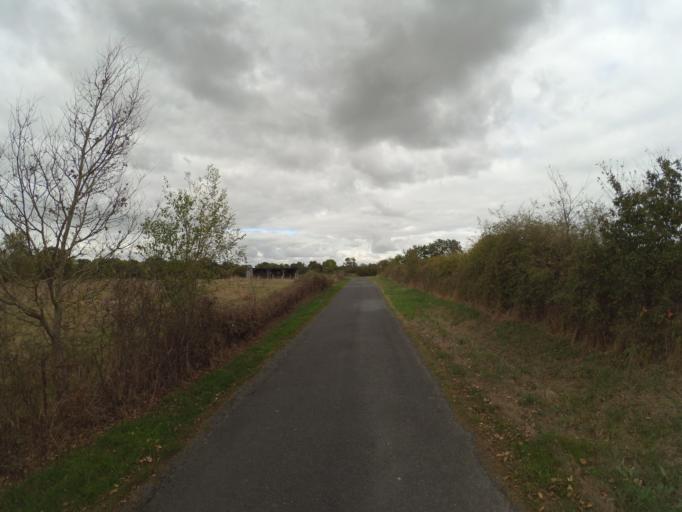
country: FR
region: Pays de la Loire
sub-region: Departement de la Loire-Atlantique
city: Remouille
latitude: 47.0525
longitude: -1.3473
